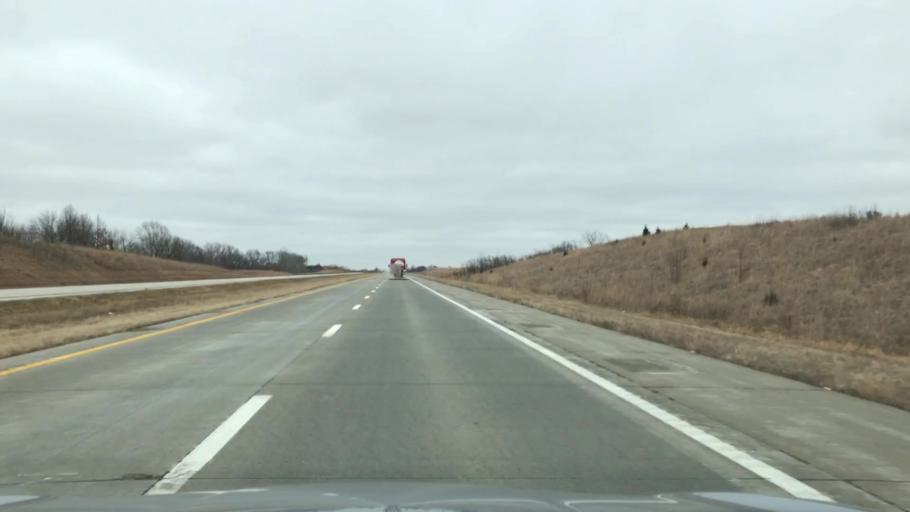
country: US
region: Missouri
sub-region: Caldwell County
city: Hamilton
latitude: 39.7346
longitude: -93.9571
